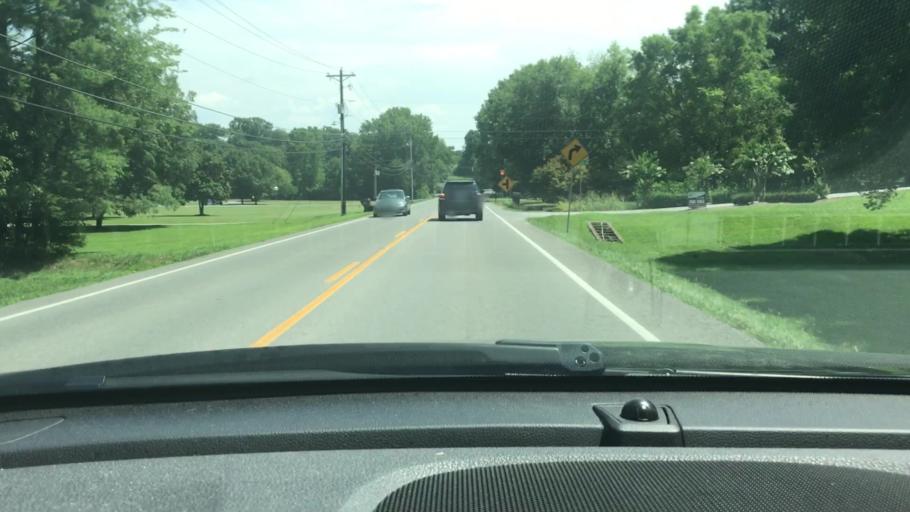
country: US
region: Tennessee
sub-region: Sumner County
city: Shackle Island
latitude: 36.3609
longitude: -86.6105
